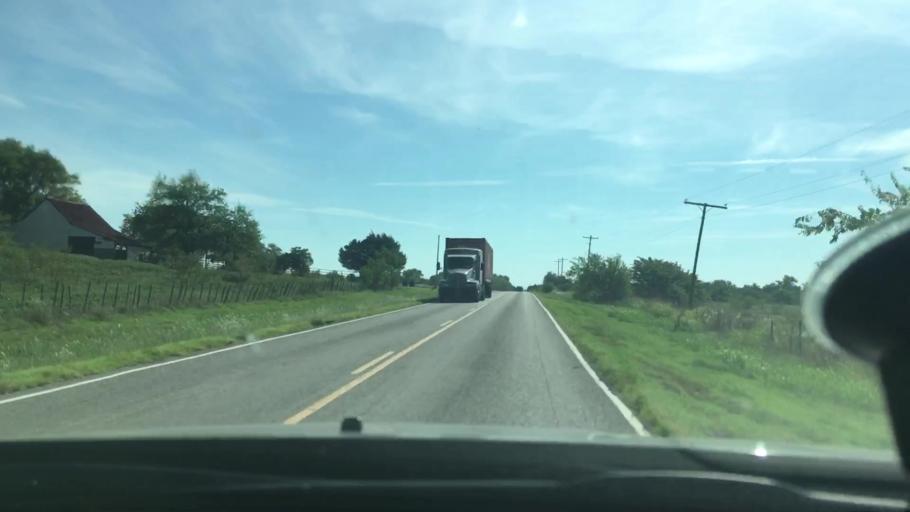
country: US
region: Oklahoma
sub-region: Carter County
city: Ardmore
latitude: 34.3327
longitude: -97.1934
